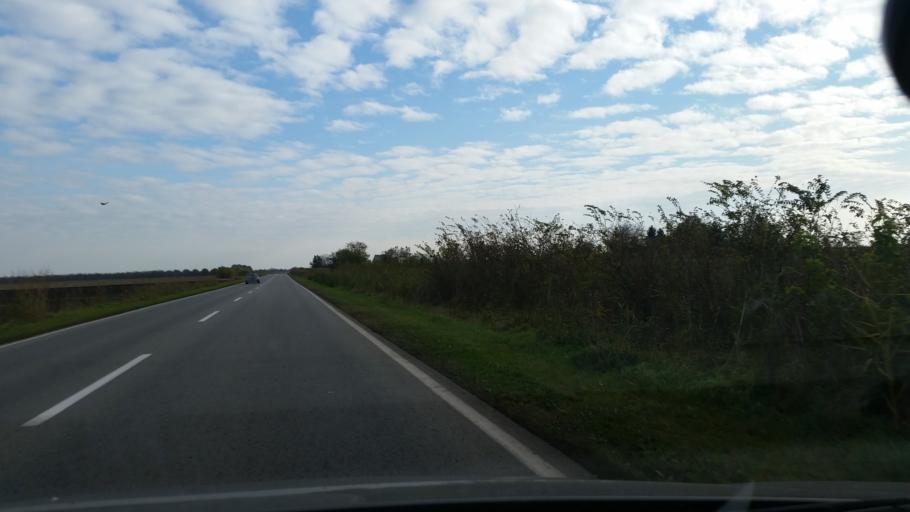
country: RS
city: Elemir
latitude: 45.4480
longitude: 20.3582
